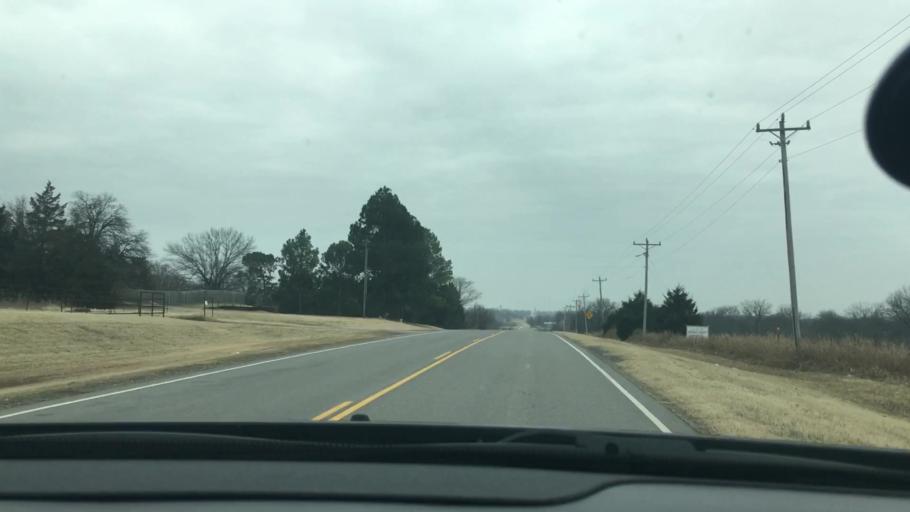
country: US
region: Oklahoma
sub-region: Carter County
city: Healdton
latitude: 34.2525
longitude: -97.4923
